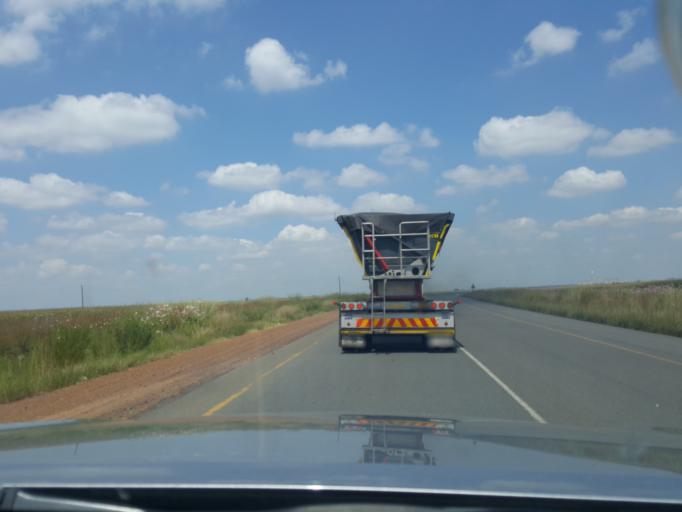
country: ZA
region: Mpumalanga
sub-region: Nkangala District Municipality
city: Witbank
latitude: -26.0167
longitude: 29.4213
